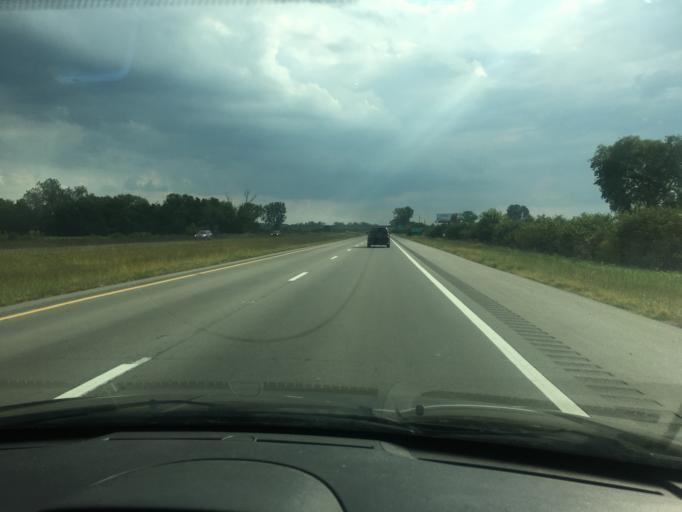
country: US
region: Ohio
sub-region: Clark County
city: Northridge
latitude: 40.0113
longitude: -83.8095
